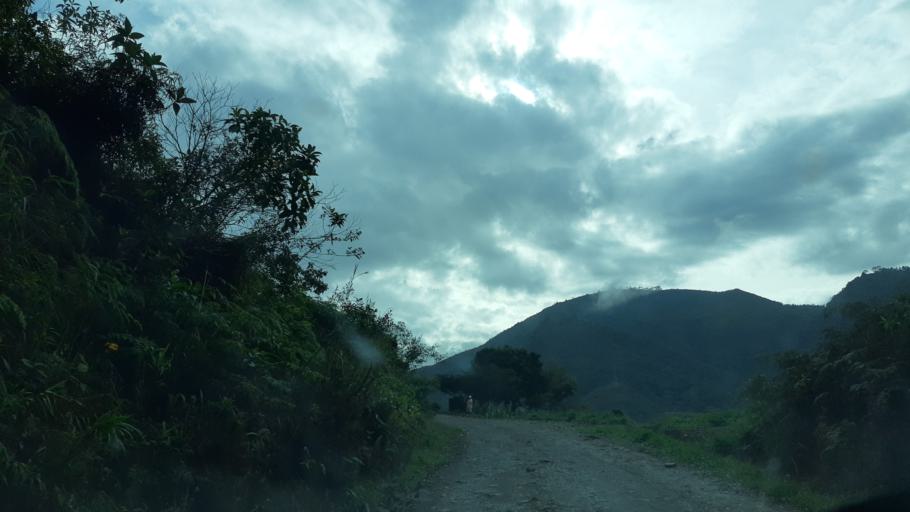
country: CO
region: Boyaca
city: Chivor
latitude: 4.9169
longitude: -73.3110
